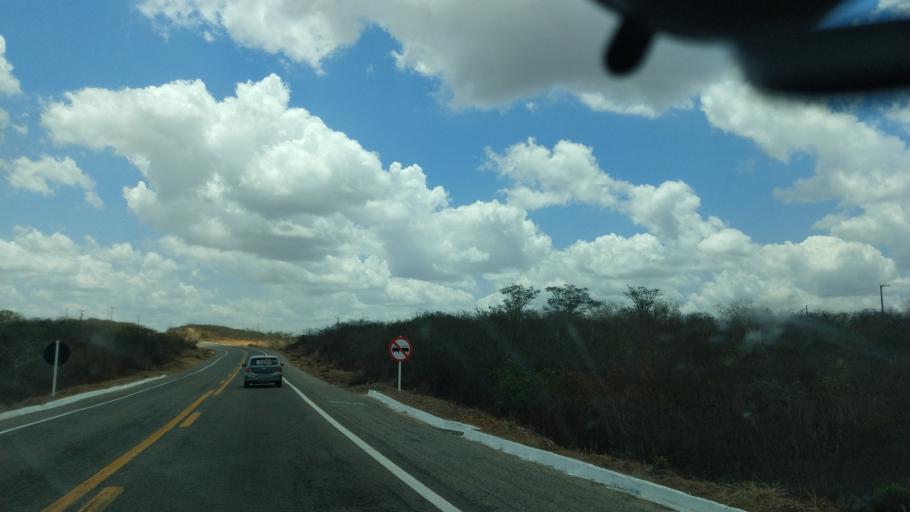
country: BR
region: Rio Grande do Norte
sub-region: Cerro Cora
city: Cerro Cora
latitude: -6.1882
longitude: -36.2349
